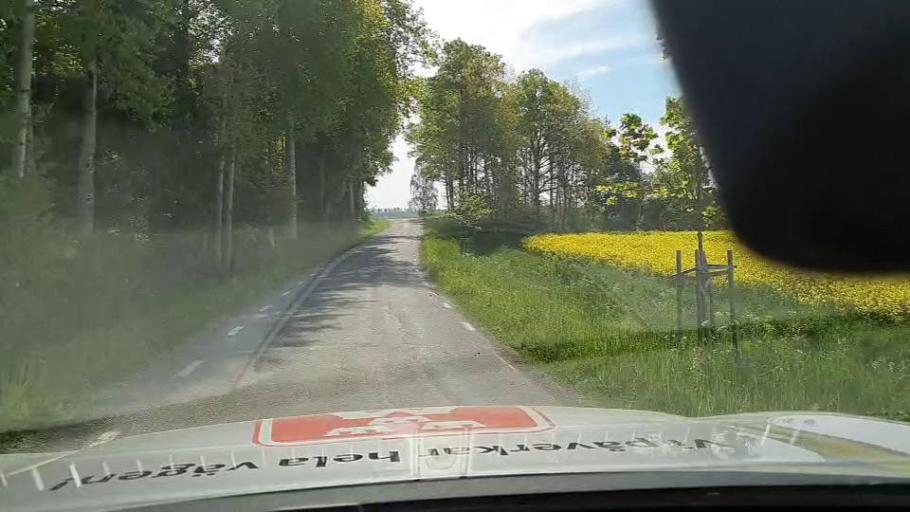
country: SE
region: Soedermanland
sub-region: Eskilstuna Kommun
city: Arla
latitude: 59.2571
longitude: 16.6812
